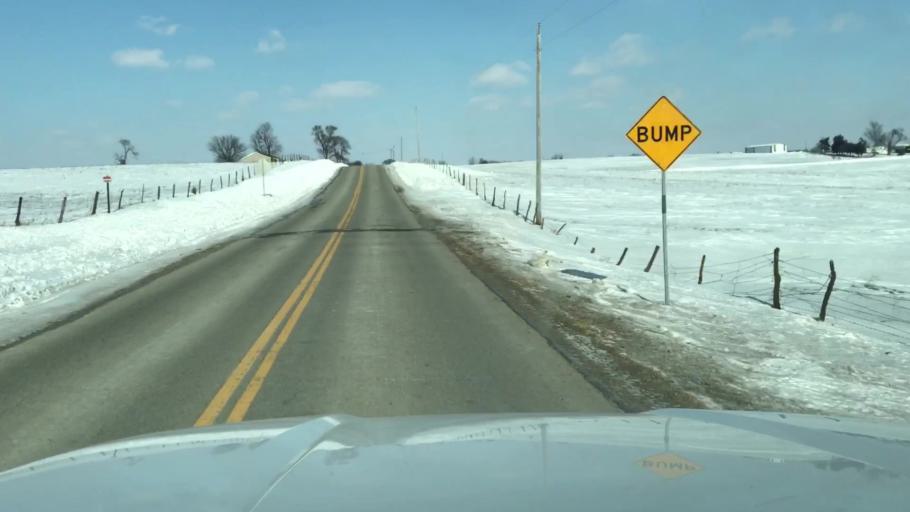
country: US
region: Missouri
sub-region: Nodaway County
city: Maryville
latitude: 40.3835
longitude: -94.7215
